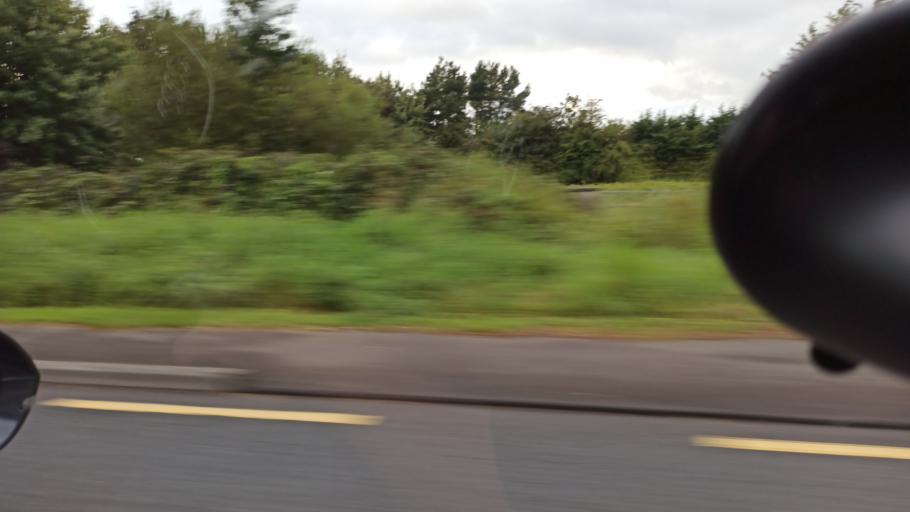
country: IE
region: Munster
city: Thurles
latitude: 52.6915
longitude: -7.8114
